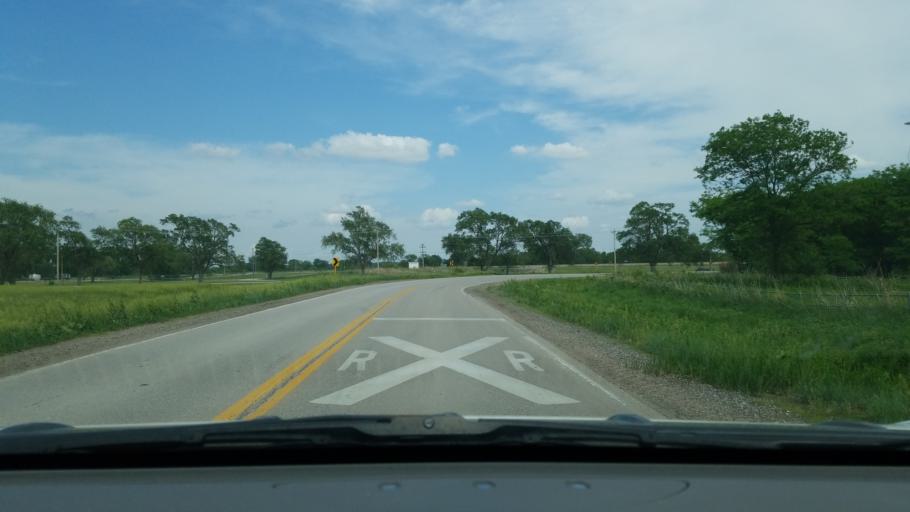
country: US
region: Nebraska
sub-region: Saunders County
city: Ashland
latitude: 41.0598
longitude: -96.3359
